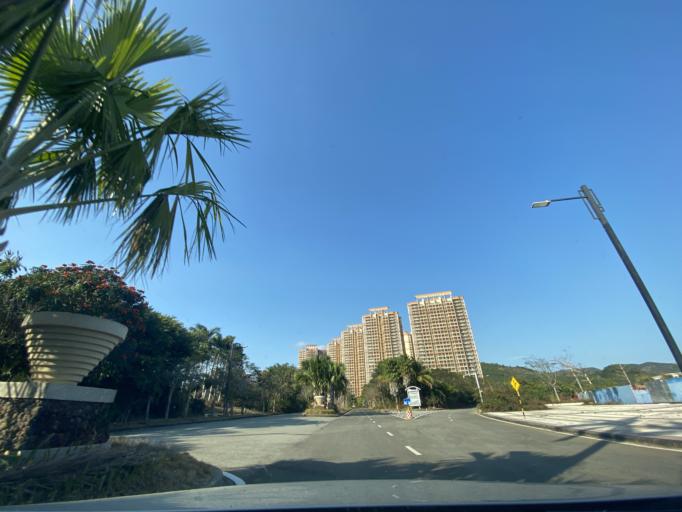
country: CN
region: Hainan
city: Yingzhou
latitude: 18.4557
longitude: 109.8556
